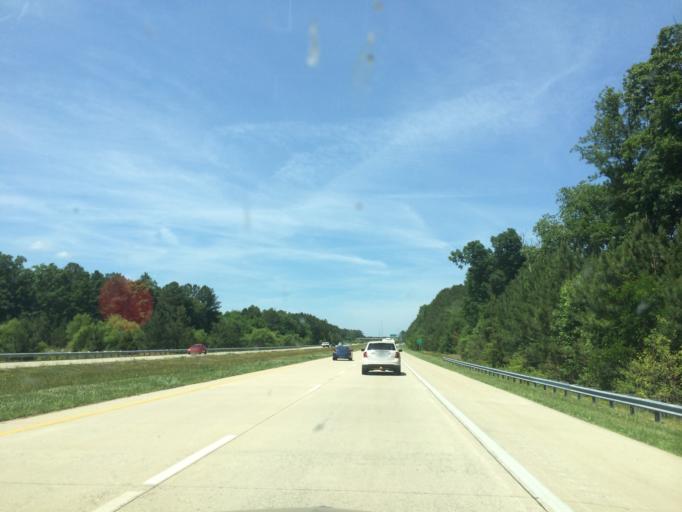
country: US
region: Maryland
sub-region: Wicomico County
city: Salisbury
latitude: 38.4040
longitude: -75.6098
